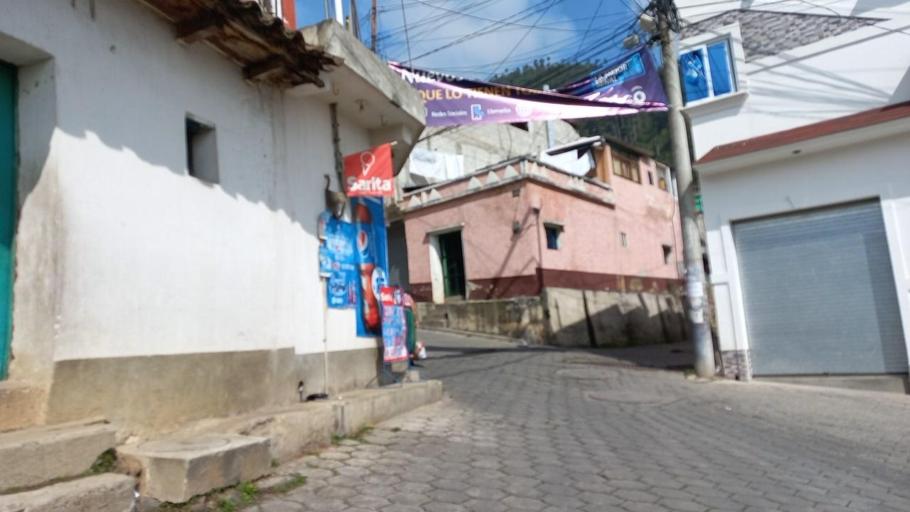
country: GT
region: Totonicapan
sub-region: Municipio de San Andres Xecul
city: San Andres Xecul
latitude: 14.9046
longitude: -91.4844
